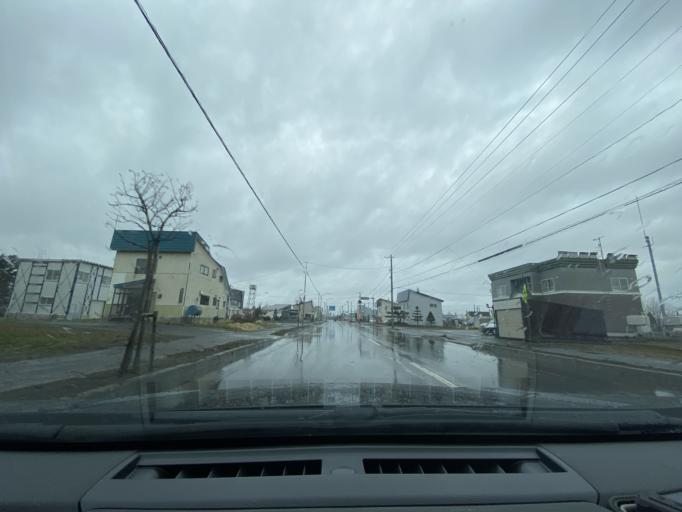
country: JP
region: Hokkaido
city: Fukagawa
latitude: 43.8089
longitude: 142.0254
